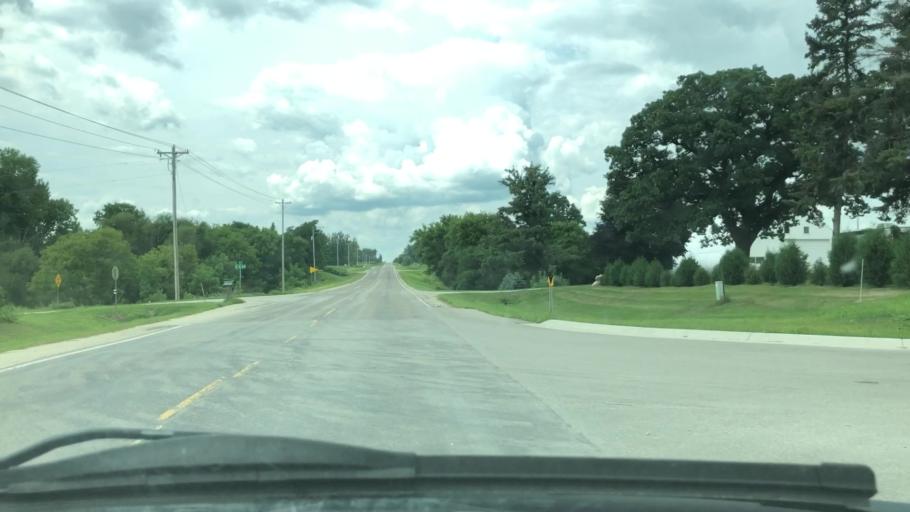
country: US
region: Minnesota
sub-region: Olmsted County
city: Stewartville
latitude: 43.8628
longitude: -92.5067
